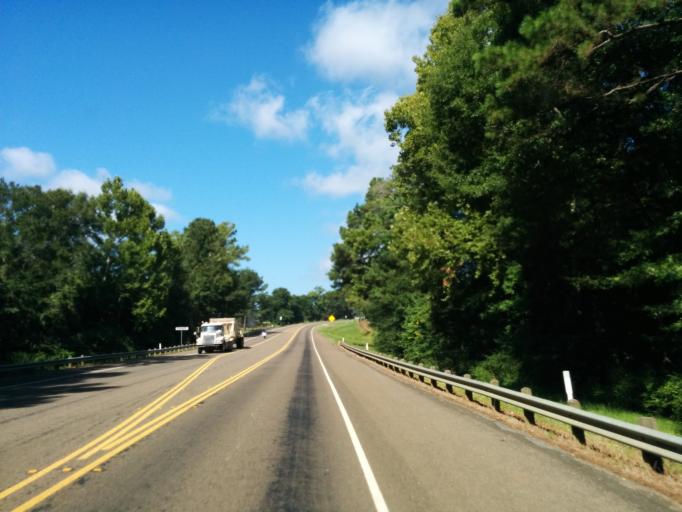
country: US
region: Texas
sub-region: Sabine County
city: Milam
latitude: 31.4139
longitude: -93.9904
